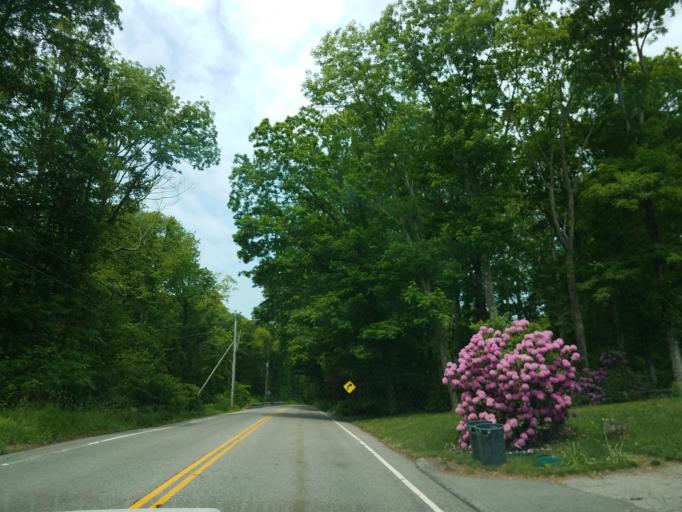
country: US
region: Rhode Island
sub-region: Washington County
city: Hopkinton
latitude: 41.5009
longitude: -71.8347
